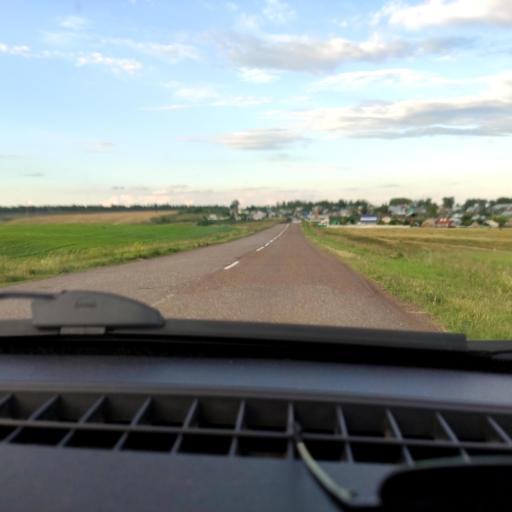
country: RU
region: Bashkortostan
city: Chishmy
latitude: 54.3984
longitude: 55.5521
